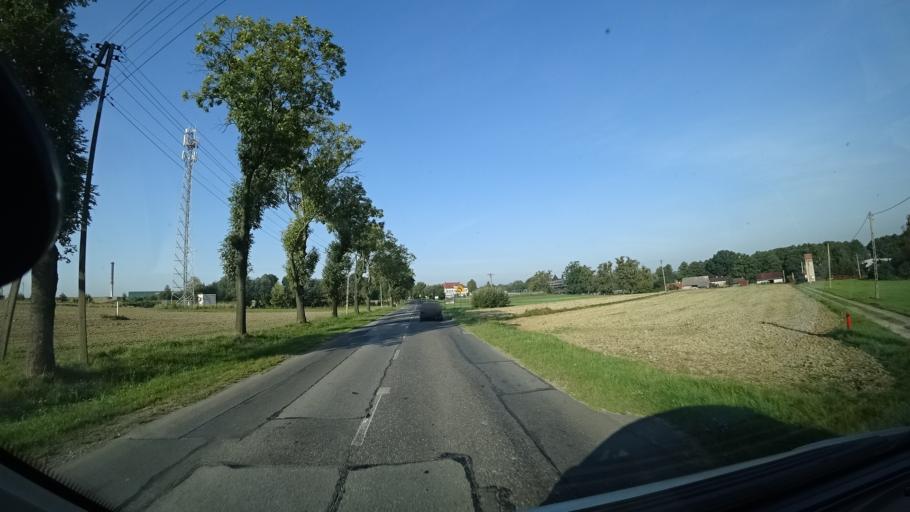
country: PL
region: Silesian Voivodeship
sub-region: Powiat gliwicki
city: Sosnicowice
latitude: 50.2792
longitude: 18.4766
